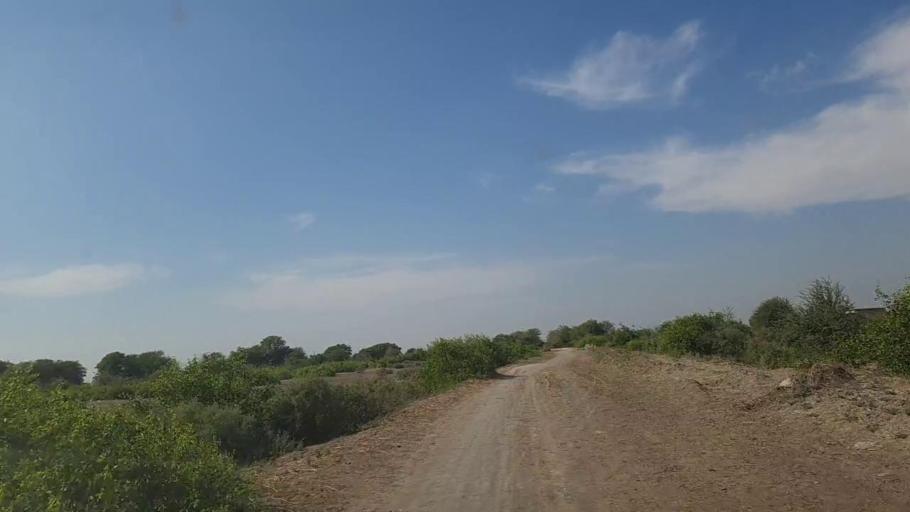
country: PK
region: Sindh
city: Mirpur Batoro
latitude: 24.8019
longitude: 68.2685
